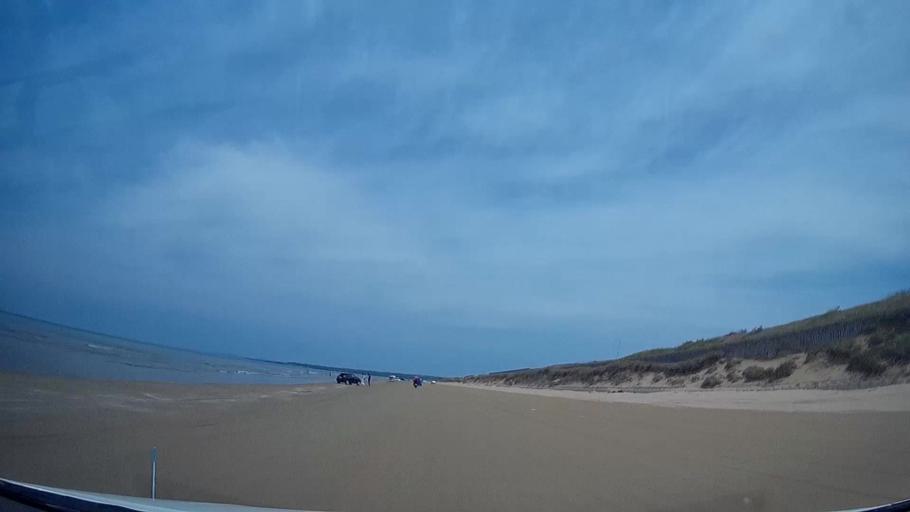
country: JP
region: Ishikawa
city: Hakui
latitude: 36.8664
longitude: 136.7585
